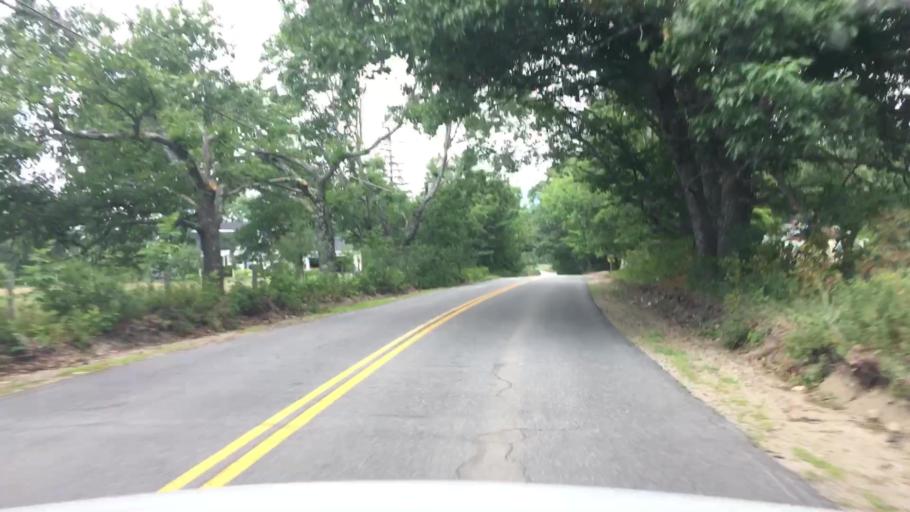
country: US
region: Maine
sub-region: Oxford County
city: Rumford
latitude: 44.5383
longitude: -70.6732
